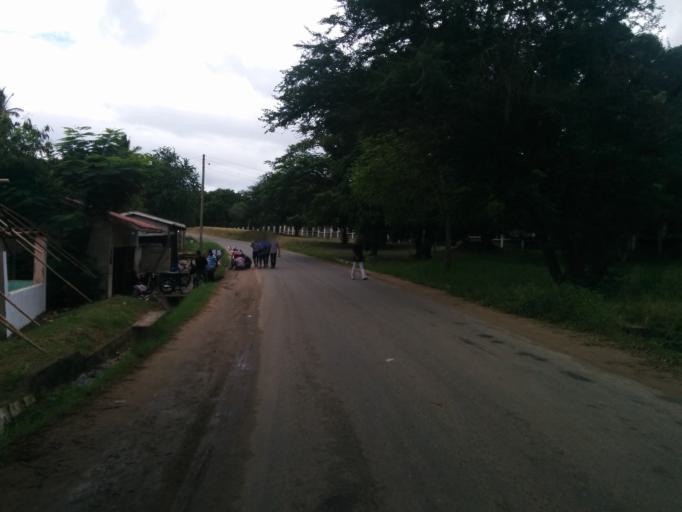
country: TZ
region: Dar es Salaam
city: Magomeni
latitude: -6.7699
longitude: 39.1945
